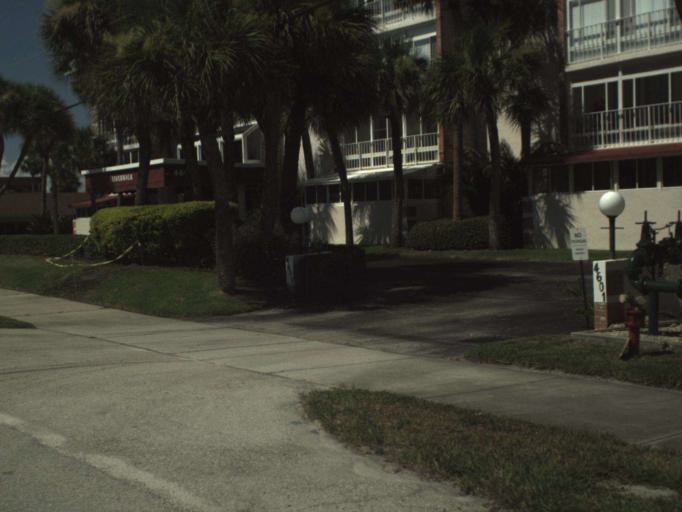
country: US
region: Florida
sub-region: Indian River County
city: Vero Beach
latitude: 27.6686
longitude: -80.3611
